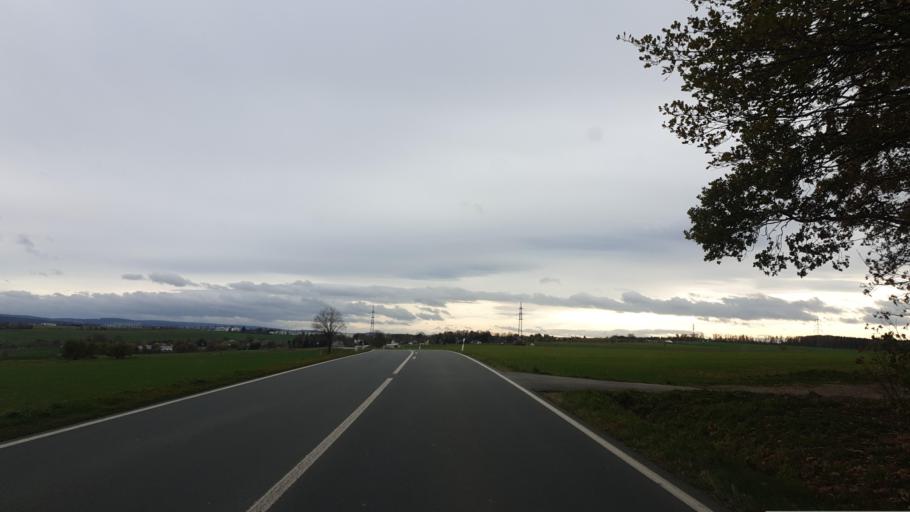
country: DE
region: Saxony
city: Limbach
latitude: 50.5732
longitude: 12.2740
